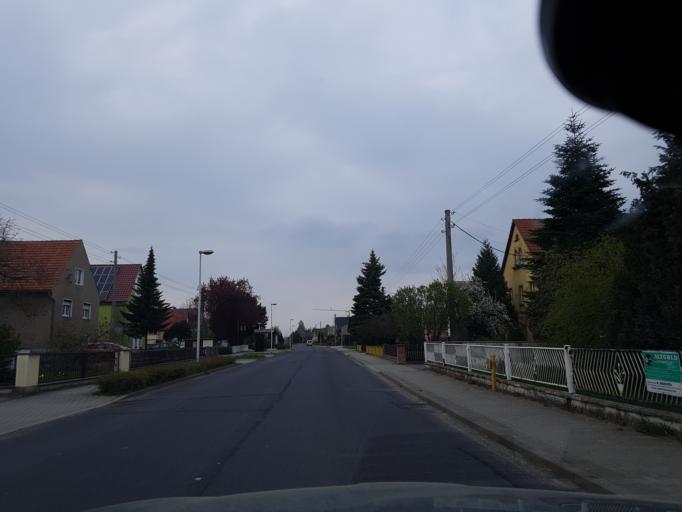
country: DE
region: Brandenburg
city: Grosskmehlen
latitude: 51.3855
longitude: 13.7115
